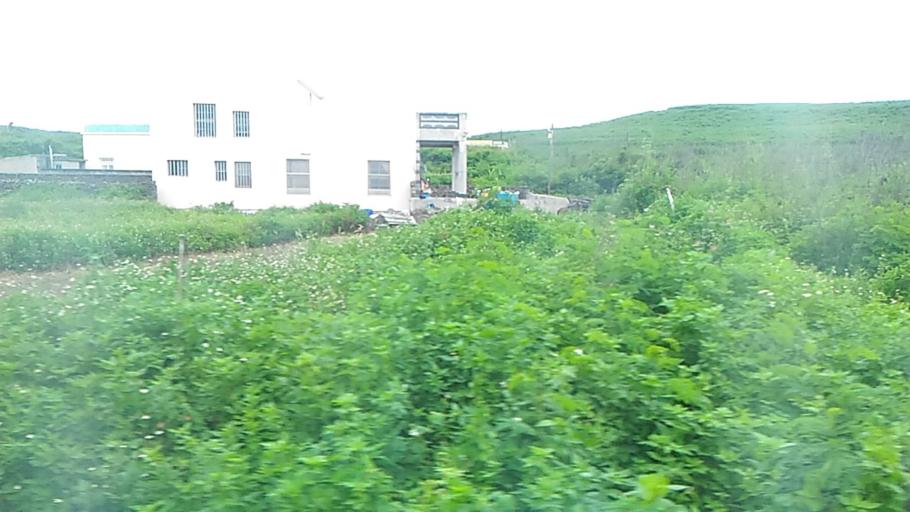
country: TW
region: Taiwan
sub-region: Penghu
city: Ma-kung
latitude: 23.2070
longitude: 119.4337
